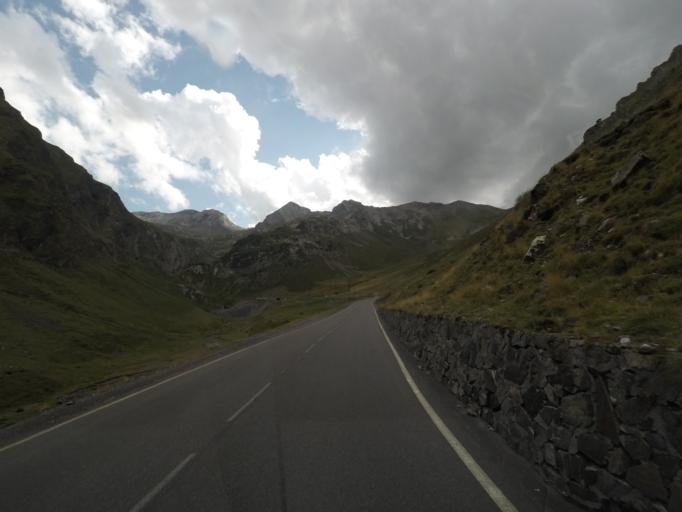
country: ES
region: Aragon
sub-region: Provincia de Huesca
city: Bielsa
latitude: 42.7540
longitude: 0.1920
